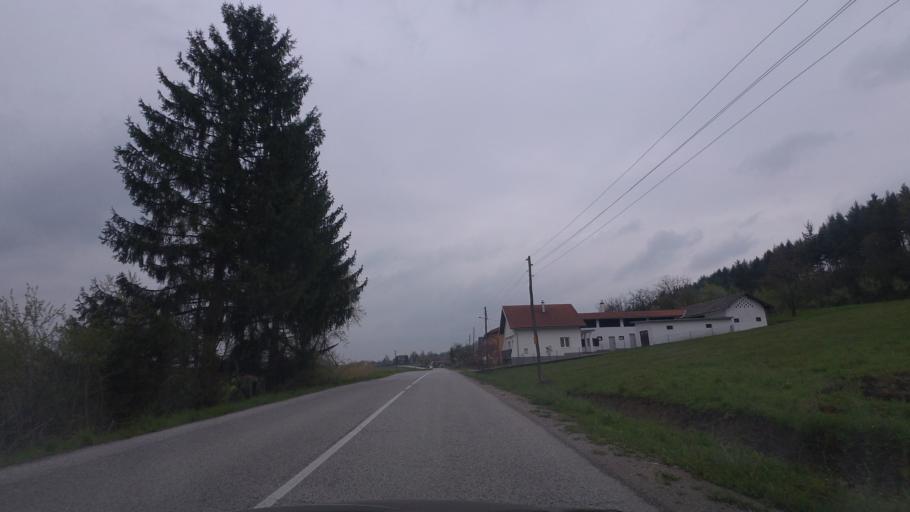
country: HR
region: Zagrebacka
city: Jastrebarsko
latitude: 45.6221
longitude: 15.5618
